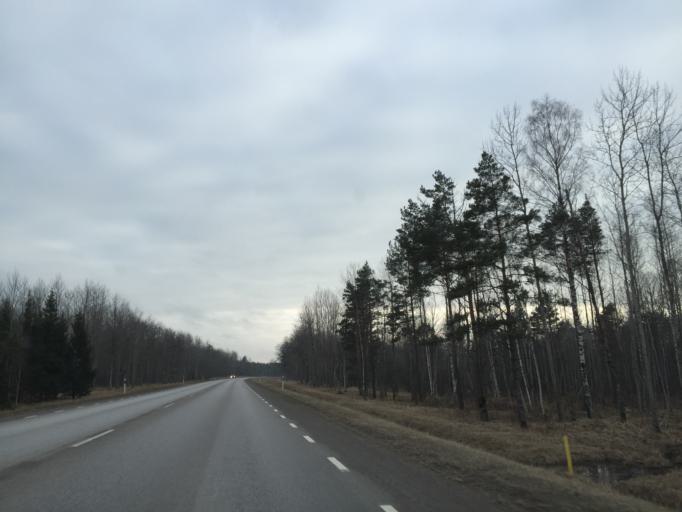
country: EE
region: Saare
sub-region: Orissaare vald
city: Orissaare
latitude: 58.4667
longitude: 22.8145
